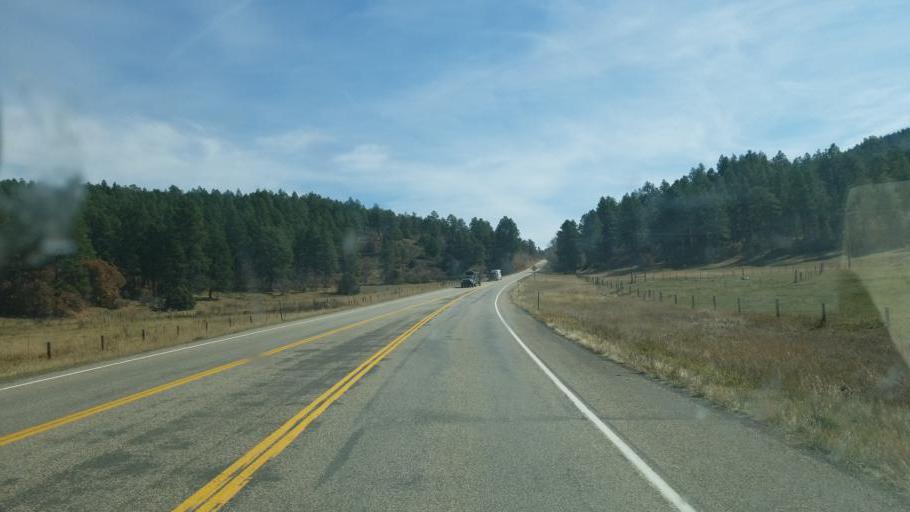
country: US
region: New Mexico
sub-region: Rio Arriba County
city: Dulce
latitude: 37.0807
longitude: -106.8639
